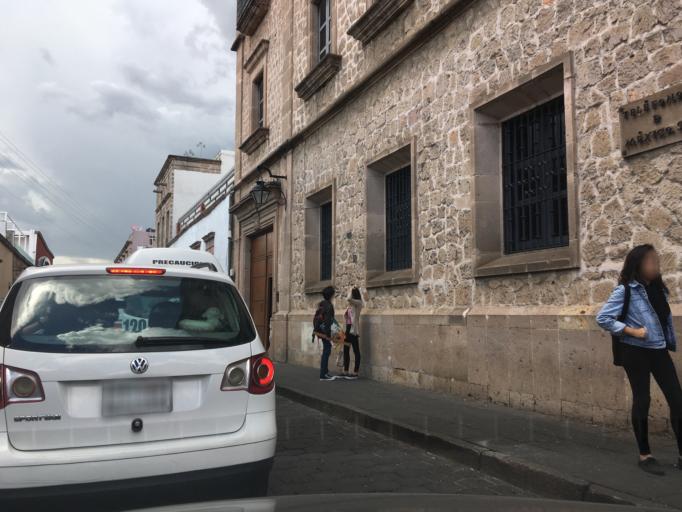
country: MX
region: Michoacan
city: Morelia
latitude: 19.7039
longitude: -101.1904
